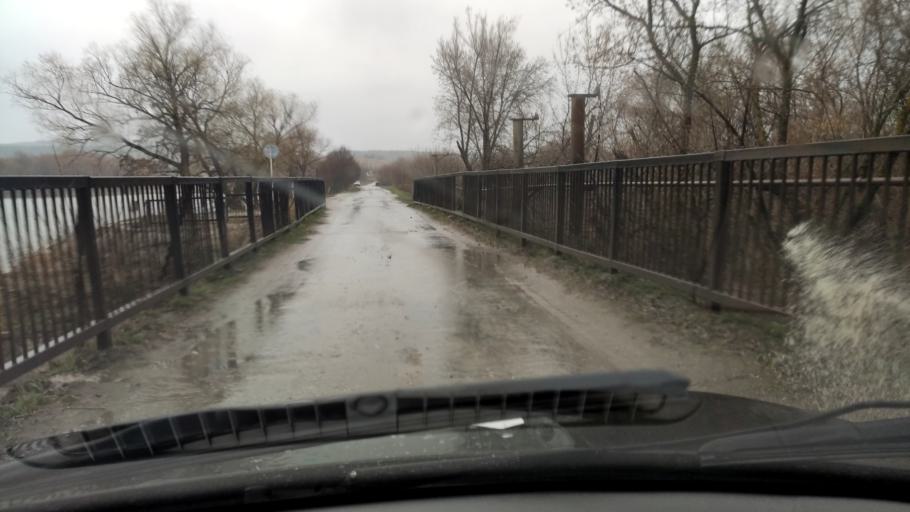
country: RU
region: Samara
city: Balasheyka
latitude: 53.2313
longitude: 48.2385
